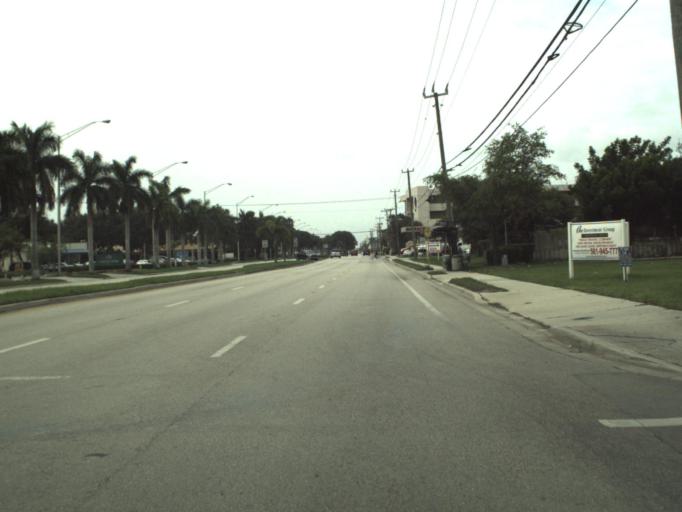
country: US
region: Florida
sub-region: Broward County
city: Pompano Beach Highlands
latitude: 26.2916
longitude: -80.0953
